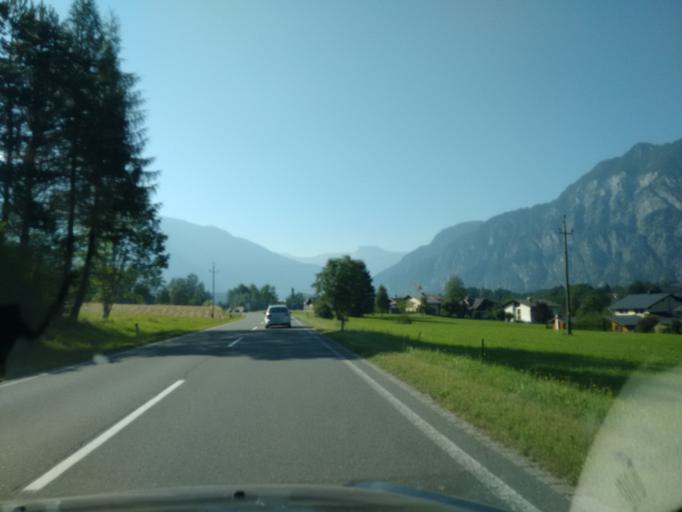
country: AT
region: Upper Austria
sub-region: Politischer Bezirk Gmunden
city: Bad Goisern
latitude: 47.6380
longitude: 13.6233
